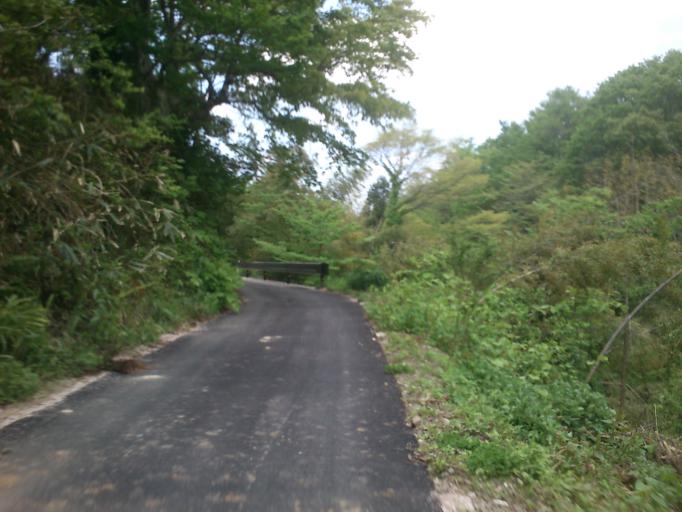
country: JP
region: Kyoto
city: Miyazu
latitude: 35.6492
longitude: 135.1556
